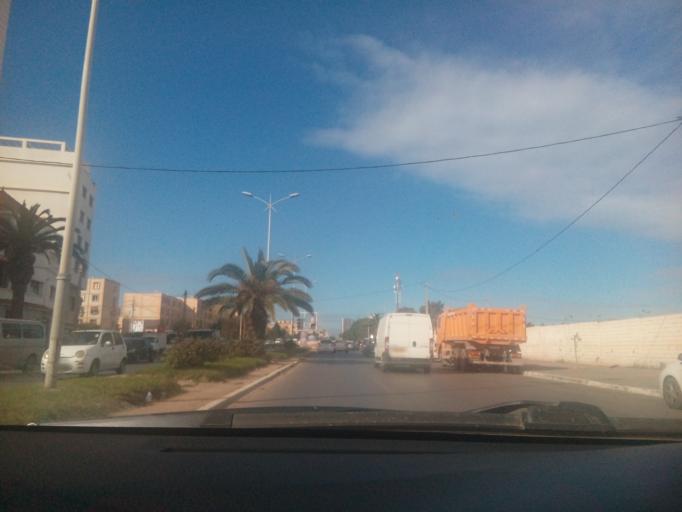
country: DZ
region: Oran
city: Oran
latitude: 35.6867
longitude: -0.6146
